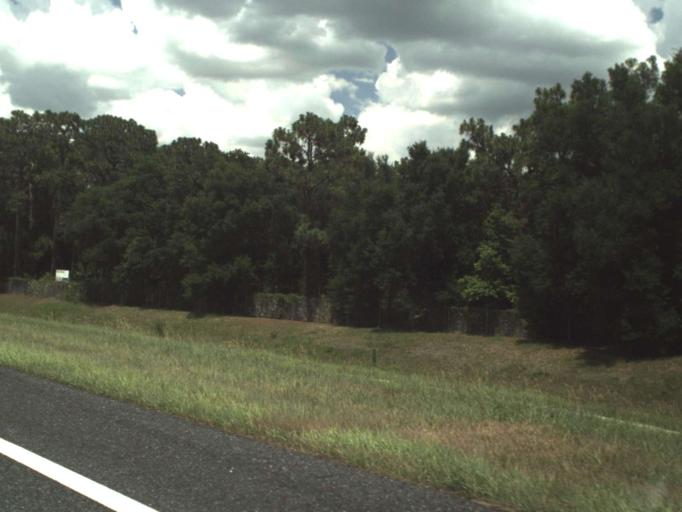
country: US
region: Florida
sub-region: Orange County
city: Fairview Shores
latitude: 28.5658
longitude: -81.4147
